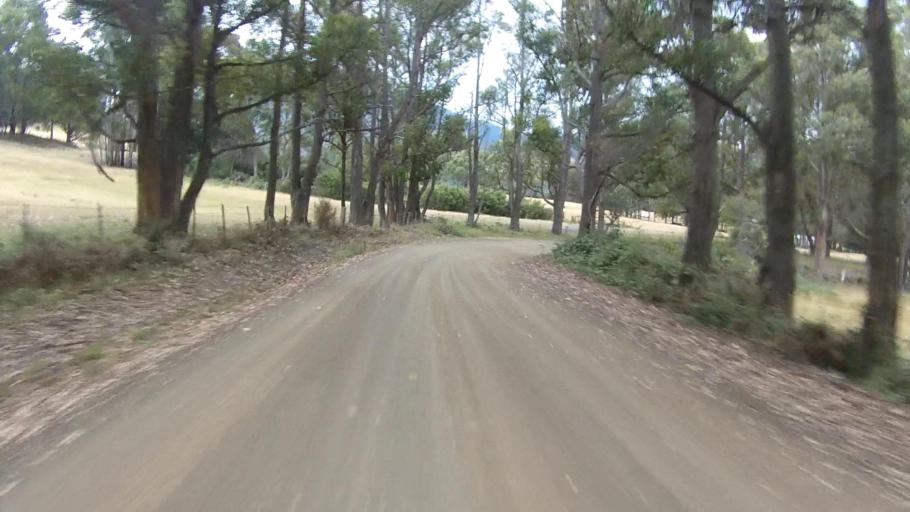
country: AU
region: Tasmania
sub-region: Huon Valley
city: Huonville
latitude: -42.9636
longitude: 147.0774
